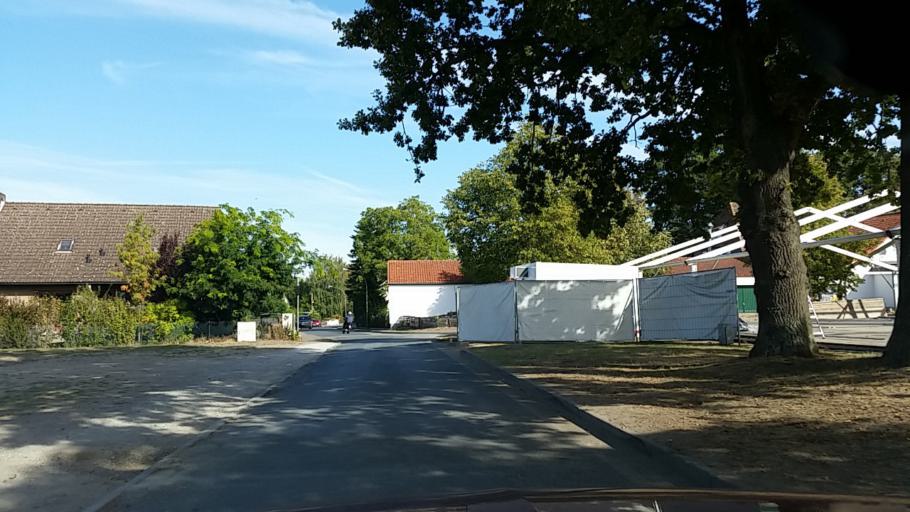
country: DE
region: Lower Saxony
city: Weyhausen
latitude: 52.4094
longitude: 10.7171
